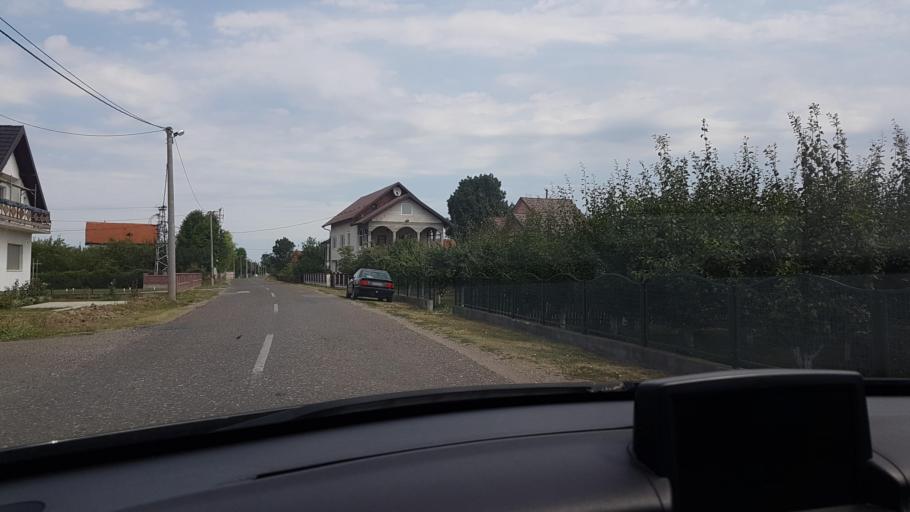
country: BA
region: Republika Srpska
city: Dvorovi
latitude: 44.8141
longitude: 19.2175
